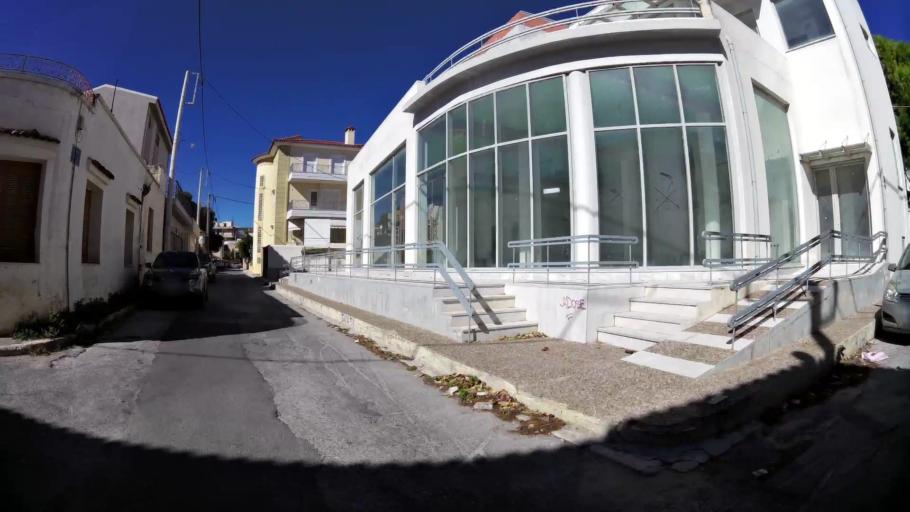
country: GR
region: Attica
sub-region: Nomarchia Anatolikis Attikis
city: Koropi
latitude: 37.8977
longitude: 23.8768
